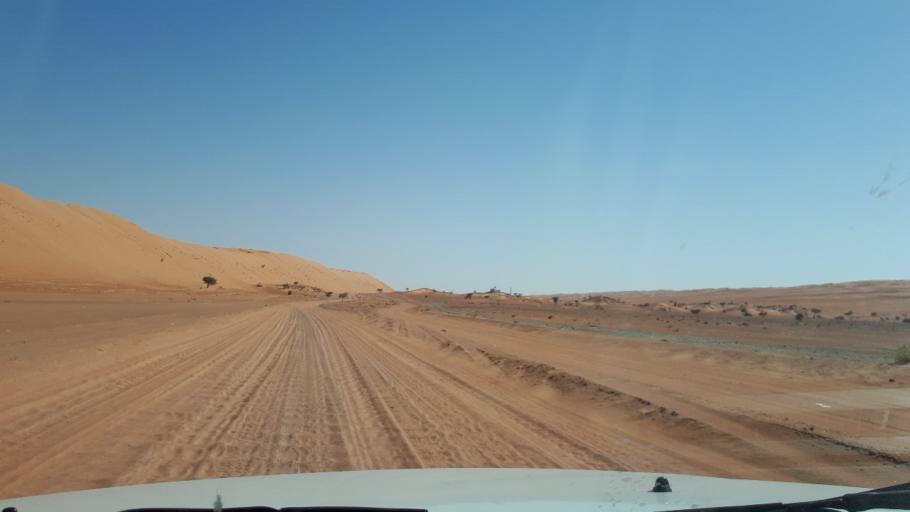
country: OM
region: Ash Sharqiyah
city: Badiyah
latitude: 22.4679
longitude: 58.7433
